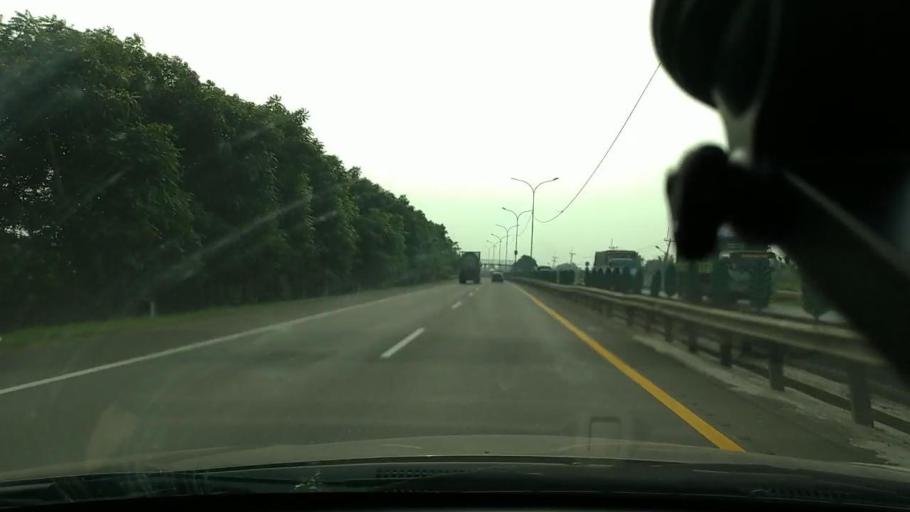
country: ID
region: Banten
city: Serang
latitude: -6.1021
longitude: 106.1733
